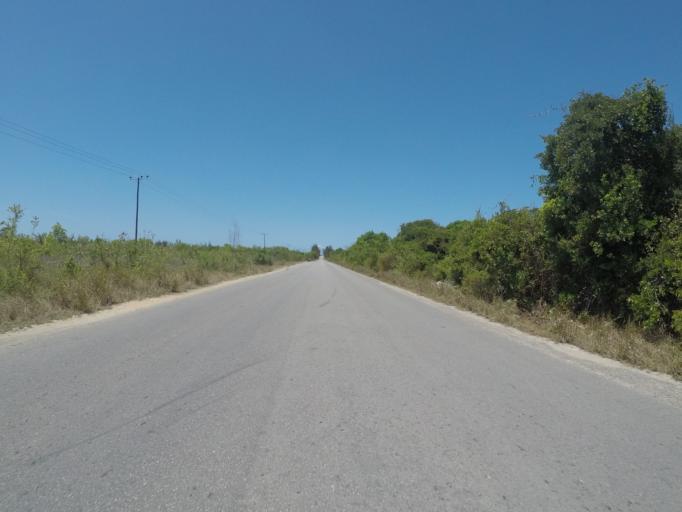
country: TZ
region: Zanzibar Central/South
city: Nganane
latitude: -6.2699
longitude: 39.5106
